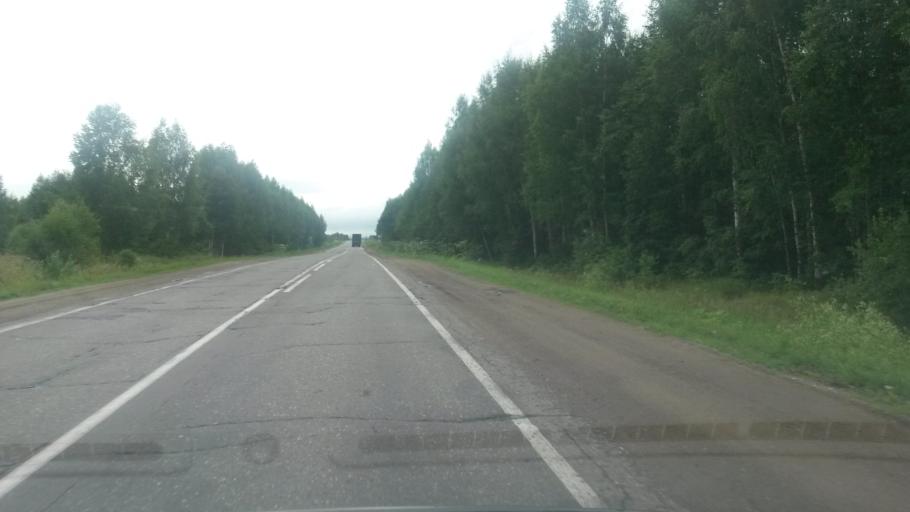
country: RU
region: Jaroslavl
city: Dubki
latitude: 57.2503
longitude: 40.1223
